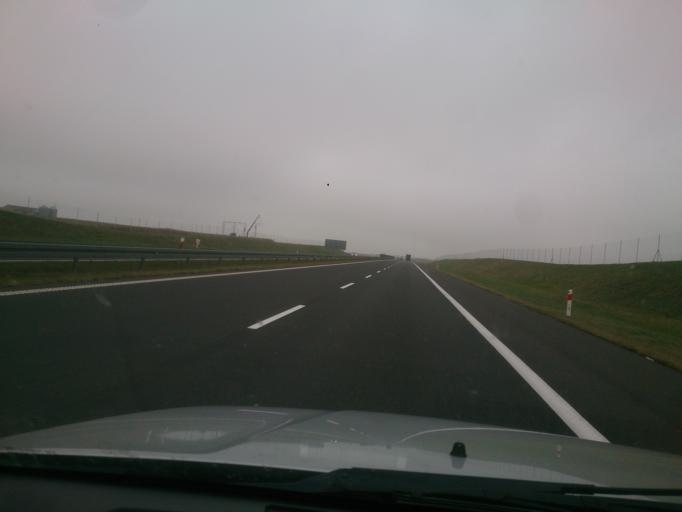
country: PL
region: Pomeranian Voivodeship
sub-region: Powiat starogardzki
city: Smetowo Graniczne
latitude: 53.7489
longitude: 18.6336
